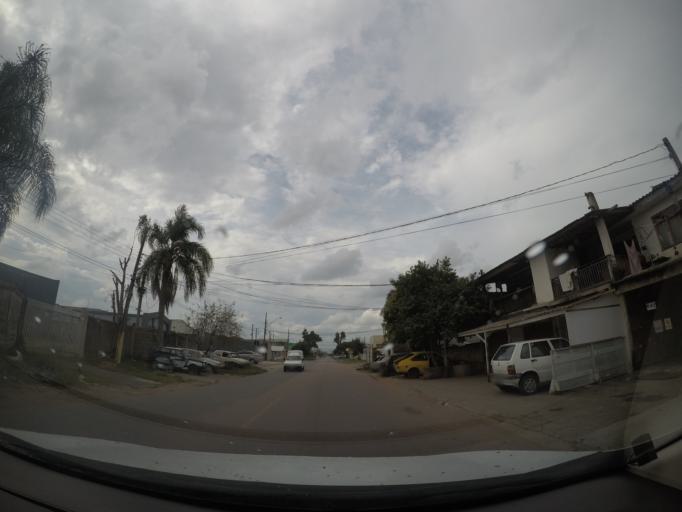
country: BR
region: Parana
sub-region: Sao Jose Dos Pinhais
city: Sao Jose dos Pinhais
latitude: -25.5036
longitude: -49.2174
